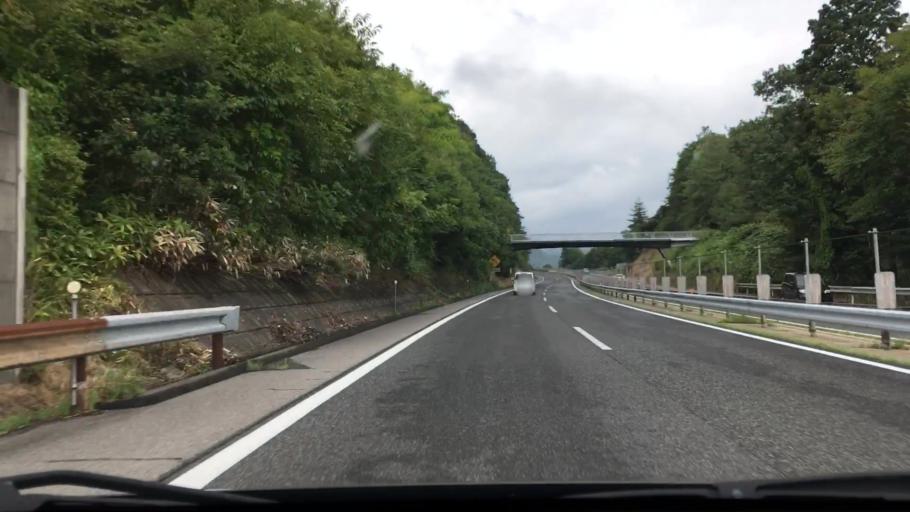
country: JP
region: Hiroshima
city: Miyoshi
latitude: 34.7181
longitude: 132.6574
